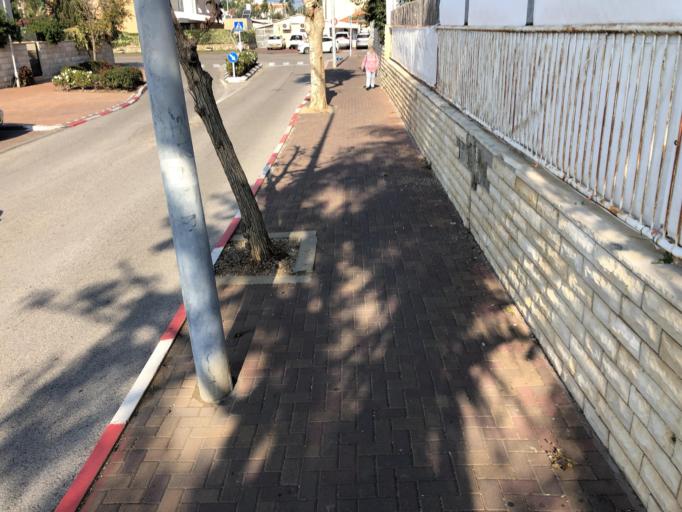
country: IL
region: Northern District
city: `Akko
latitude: 32.9274
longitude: 35.0948
